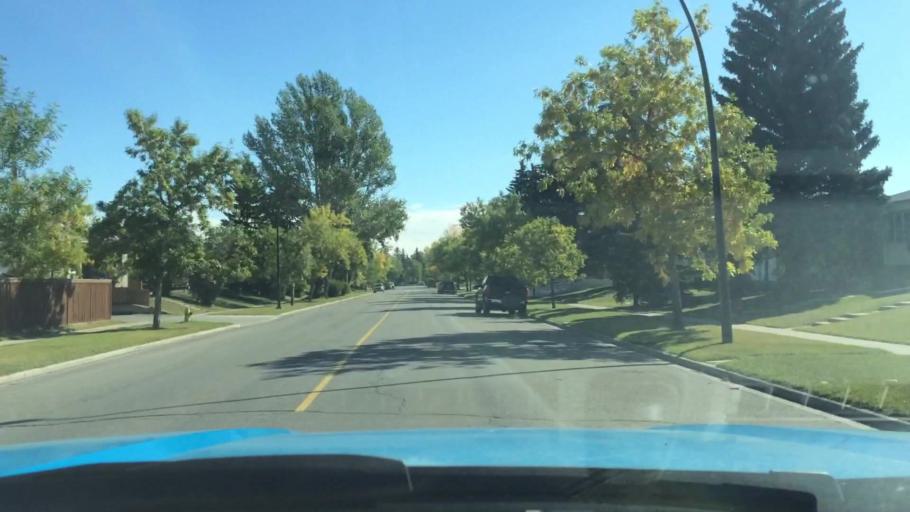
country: CA
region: Alberta
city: Calgary
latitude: 51.1178
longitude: -114.0585
